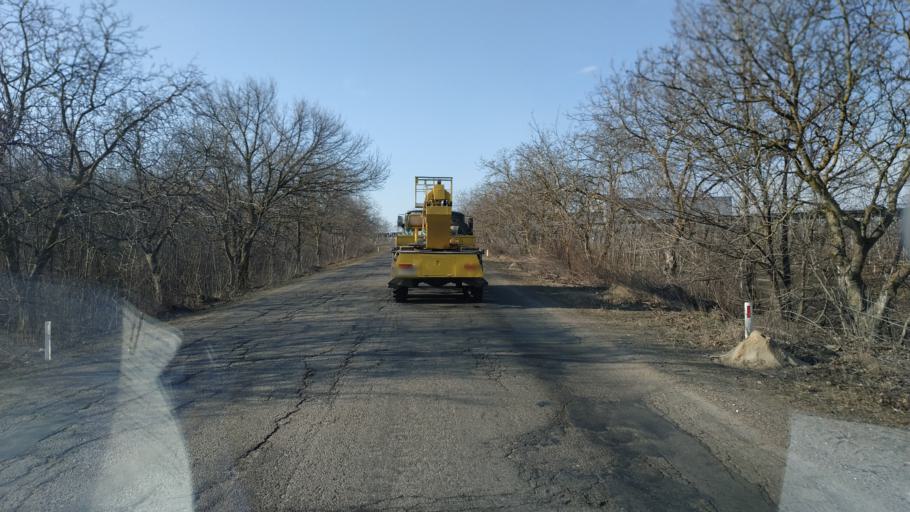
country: MD
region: Chisinau
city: Singera
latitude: 46.8644
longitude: 29.0337
